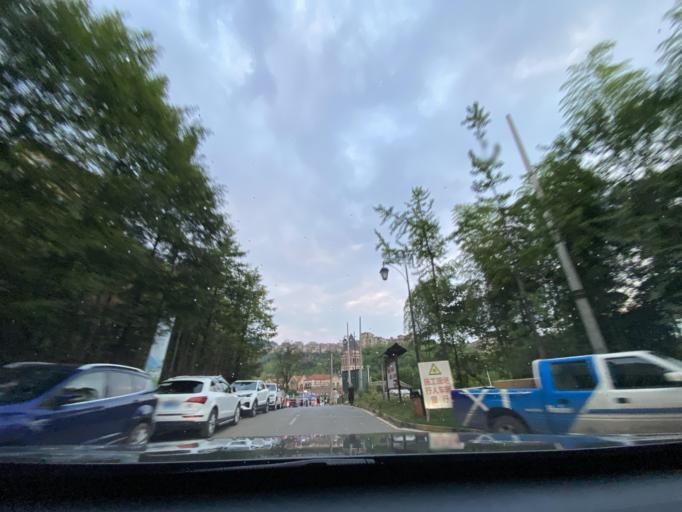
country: CN
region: Guizhou Sheng
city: Changqi
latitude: 28.5388
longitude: 105.9878
